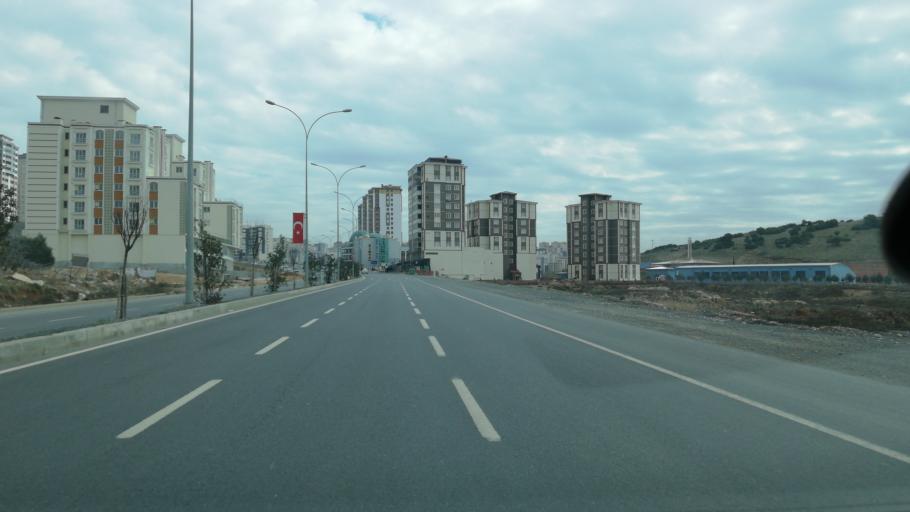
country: TR
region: Kahramanmaras
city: Kahramanmaras
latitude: 37.5869
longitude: 36.8457
